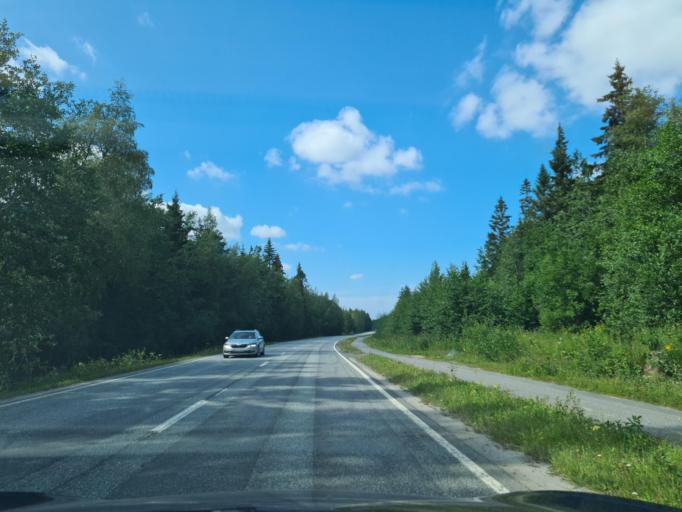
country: FI
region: Ostrobothnia
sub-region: Vaasa
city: Replot
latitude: 63.1993
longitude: 21.5370
